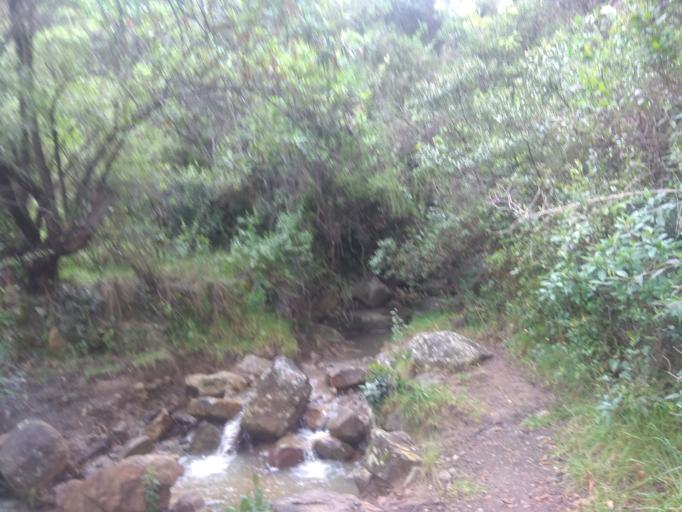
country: CO
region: Boyaca
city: Socha Viejo
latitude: 6.0082
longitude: -72.6760
